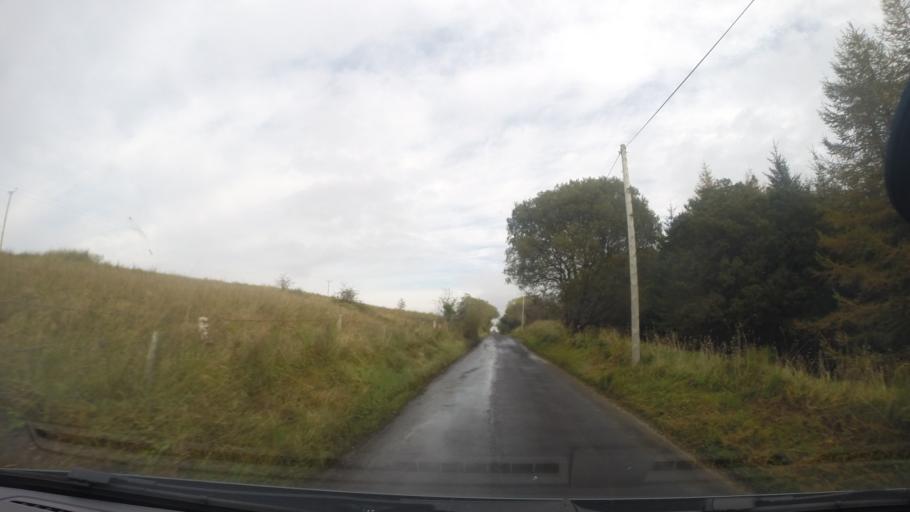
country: IE
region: Ulster
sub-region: County Donegal
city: Ballyshannon
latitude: 54.4200
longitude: -8.0059
